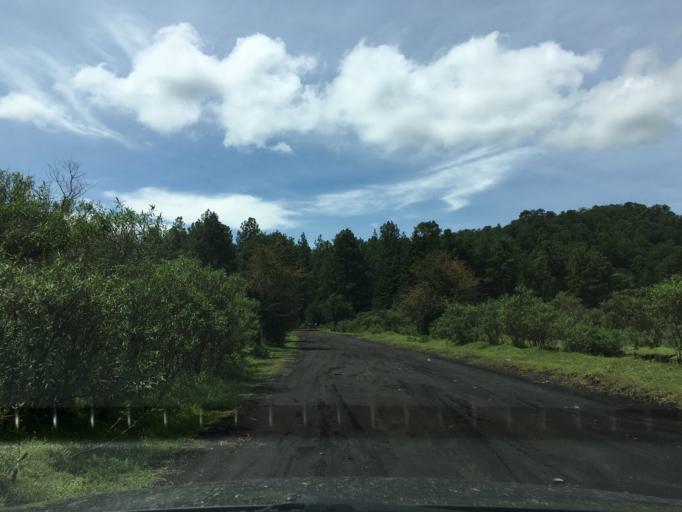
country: MX
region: Michoacan
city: Angahuan
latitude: 19.5082
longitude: -102.2124
